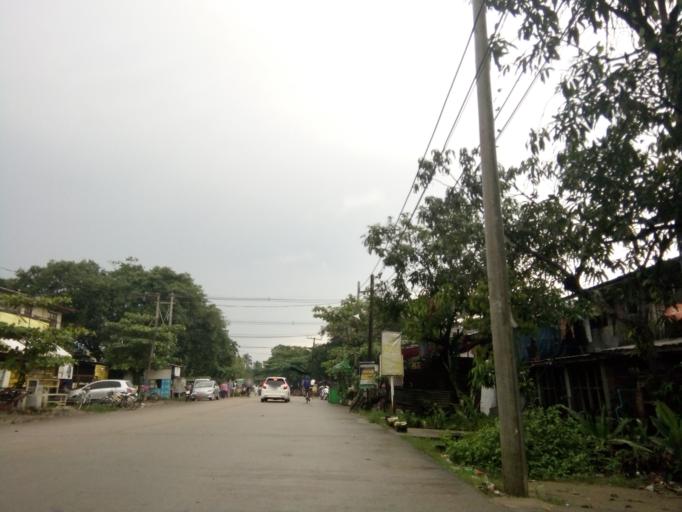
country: MM
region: Yangon
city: Yangon
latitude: 16.9166
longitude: 96.1600
